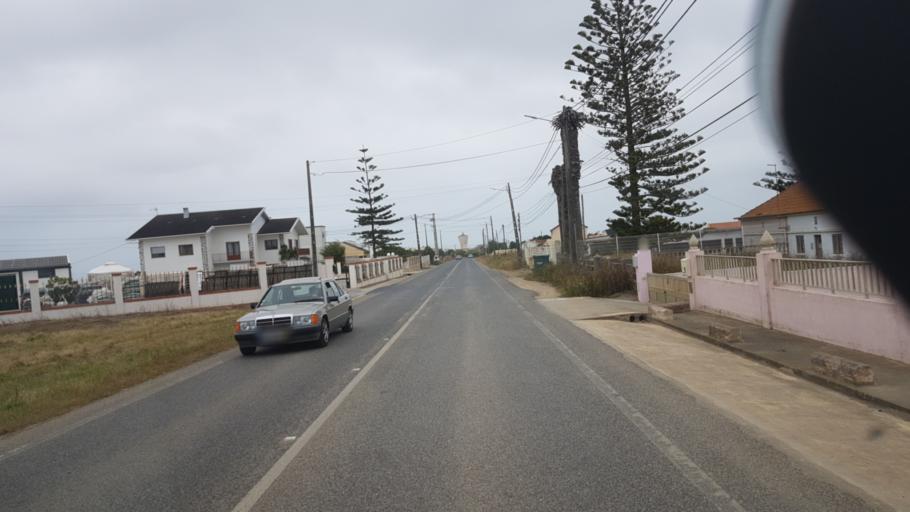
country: PT
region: Leiria
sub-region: Peniche
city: Atouguia da Baleia
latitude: 39.3357
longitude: -9.3052
